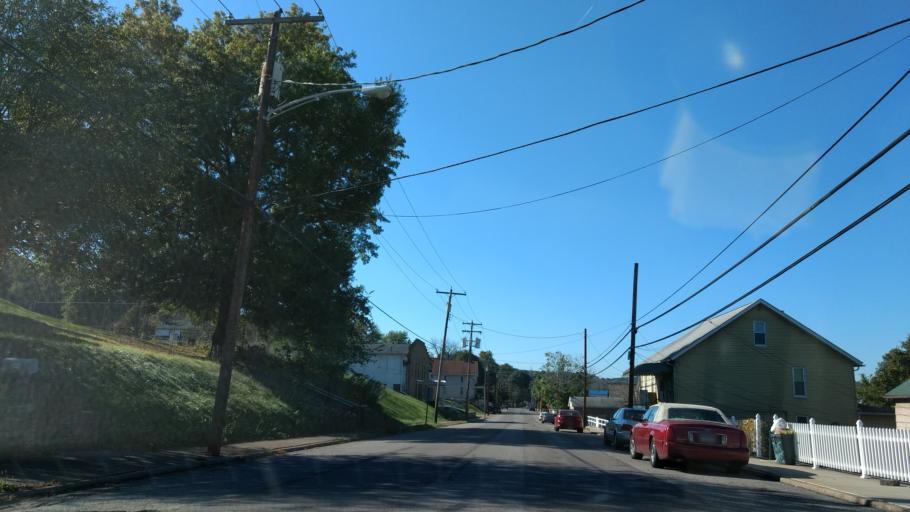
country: US
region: Pennsylvania
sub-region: Washington County
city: New Eagle
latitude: 40.2073
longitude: -79.9454
